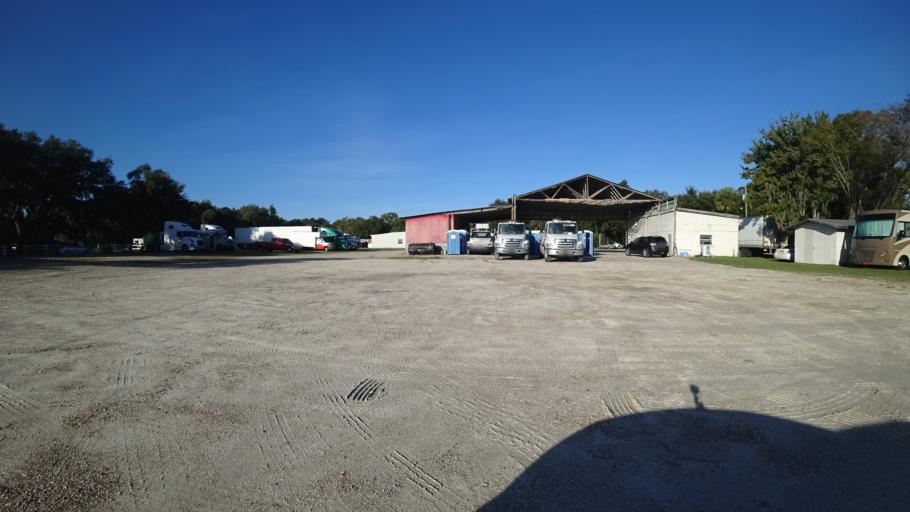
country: US
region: Florida
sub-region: Manatee County
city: Ellenton
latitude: 27.5678
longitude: -82.5223
